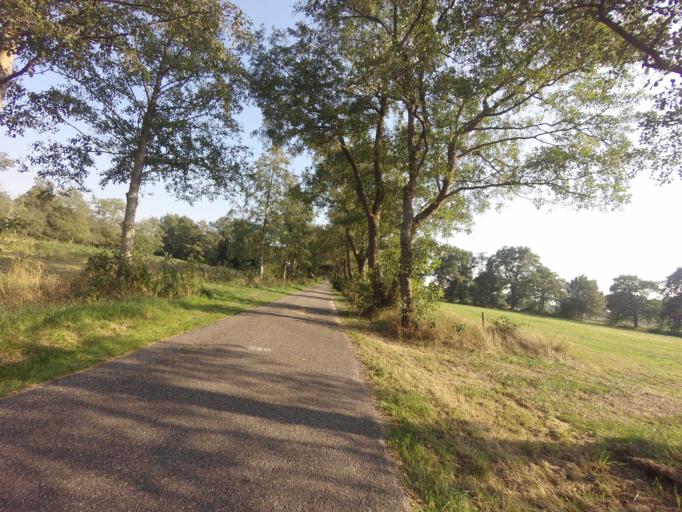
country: NL
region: Drenthe
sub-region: Gemeente Tynaarlo
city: Vries
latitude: 53.1315
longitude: 6.4895
